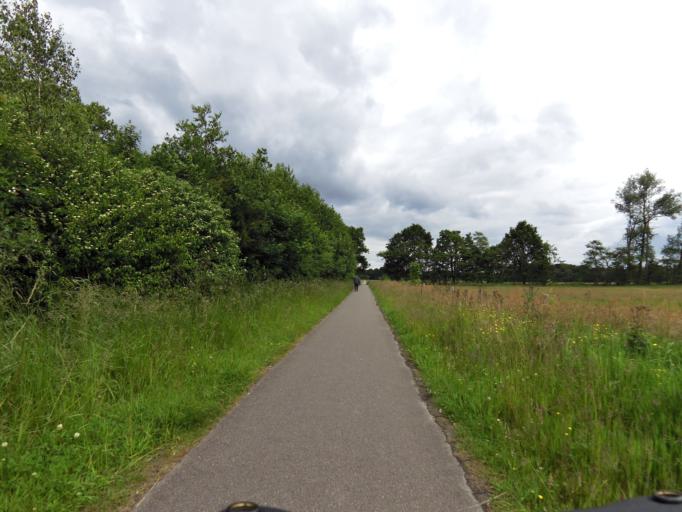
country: NL
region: North Brabant
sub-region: Gemeente Breda
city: Breda
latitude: 51.5528
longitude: 4.7855
